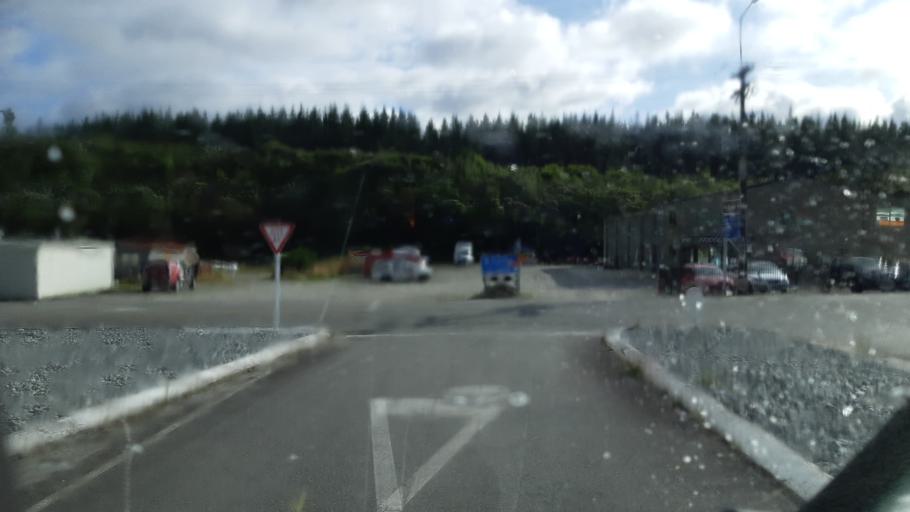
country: NZ
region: West Coast
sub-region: Westland District
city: Hokitika
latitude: -42.7452
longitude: 171.0007
